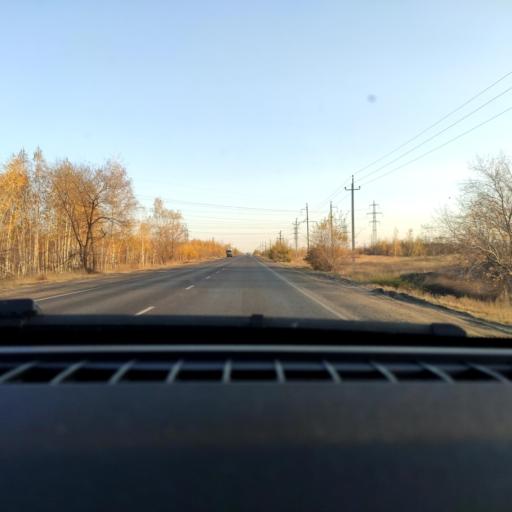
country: RU
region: Voronezj
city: Maslovka
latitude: 51.5839
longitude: 39.2583
